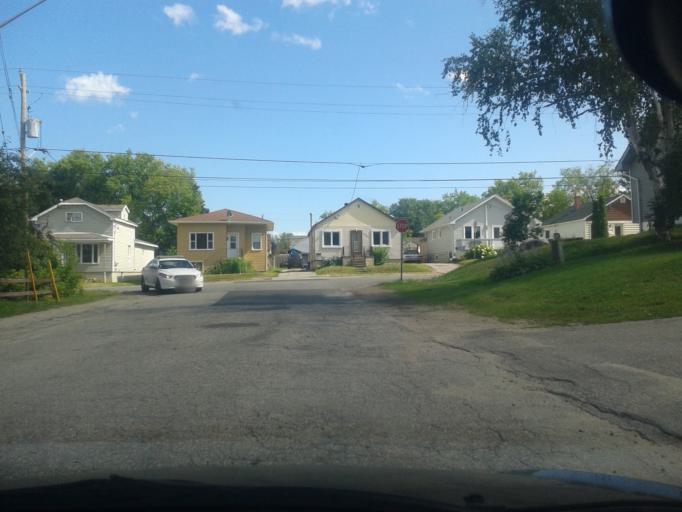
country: CA
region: Ontario
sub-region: Nipissing District
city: North Bay
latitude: 46.3102
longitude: -79.4477
